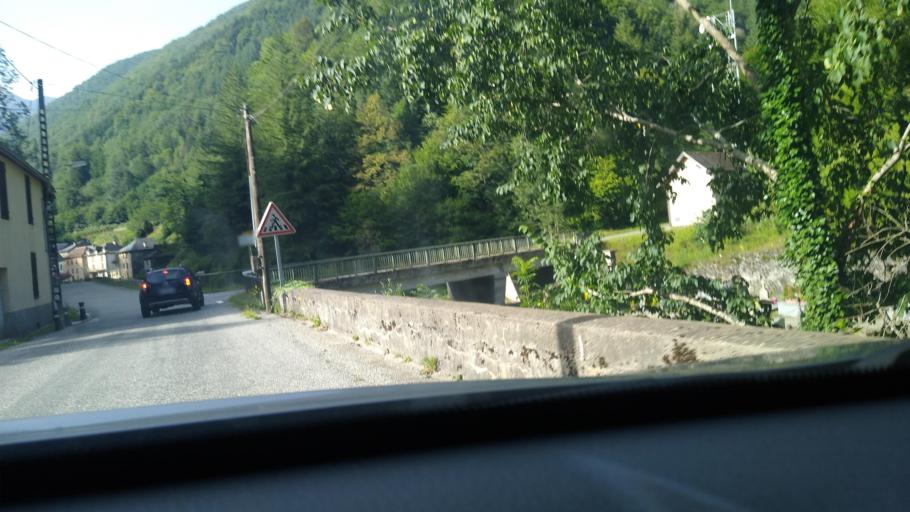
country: FR
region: Midi-Pyrenees
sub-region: Departement de l'Ariege
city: Saint-Girons
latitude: 42.7900
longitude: 1.1863
